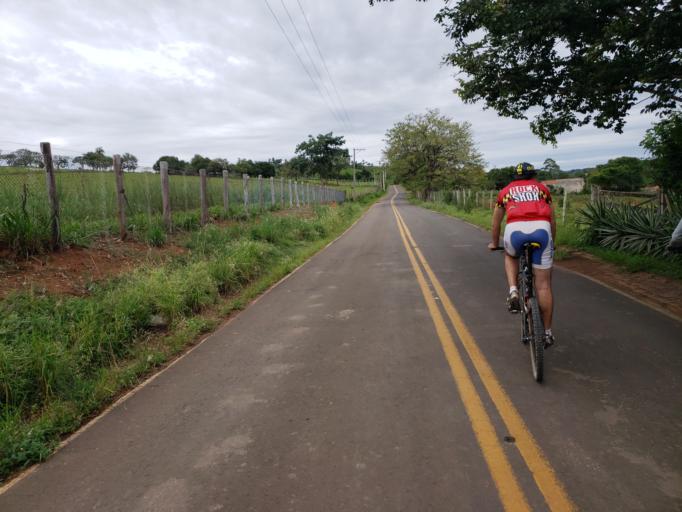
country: BR
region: Sao Paulo
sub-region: Itapira
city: Itapira
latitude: -22.3310
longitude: -46.8209
